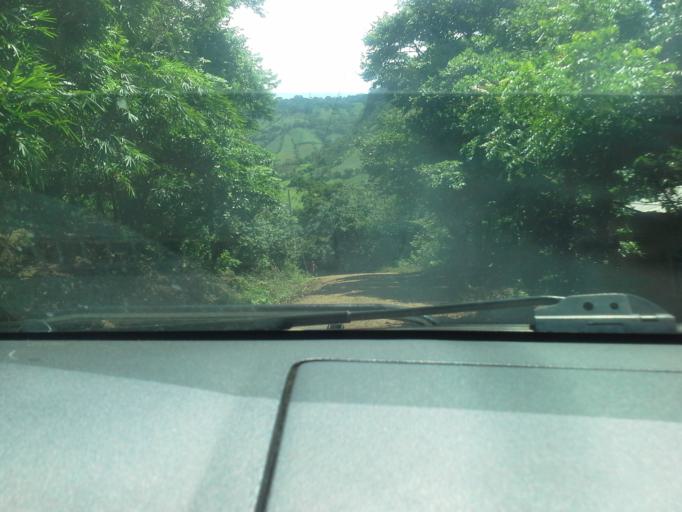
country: NI
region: Matagalpa
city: Terrabona
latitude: 12.7398
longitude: -85.9238
